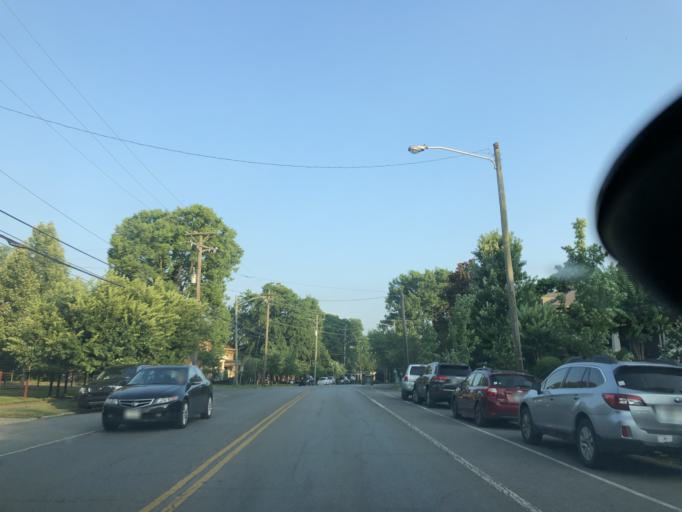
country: US
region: Tennessee
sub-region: Davidson County
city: Nashville
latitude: 36.1282
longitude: -86.7948
